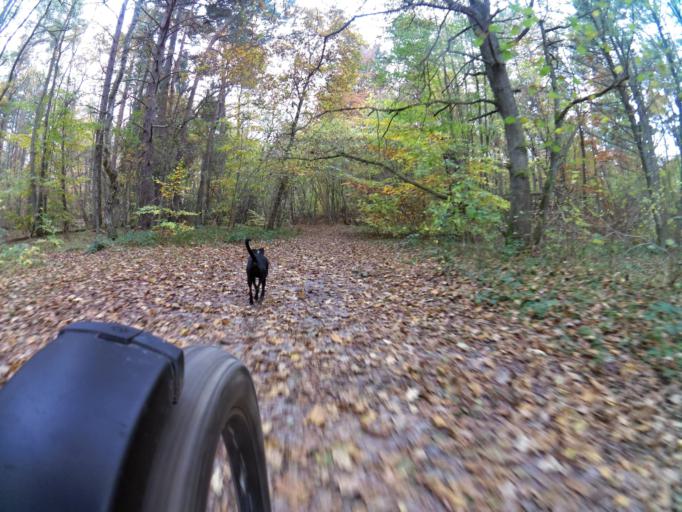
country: PL
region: Pomeranian Voivodeship
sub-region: Powiat pucki
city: Krokowa
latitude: 54.8304
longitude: 18.1436
